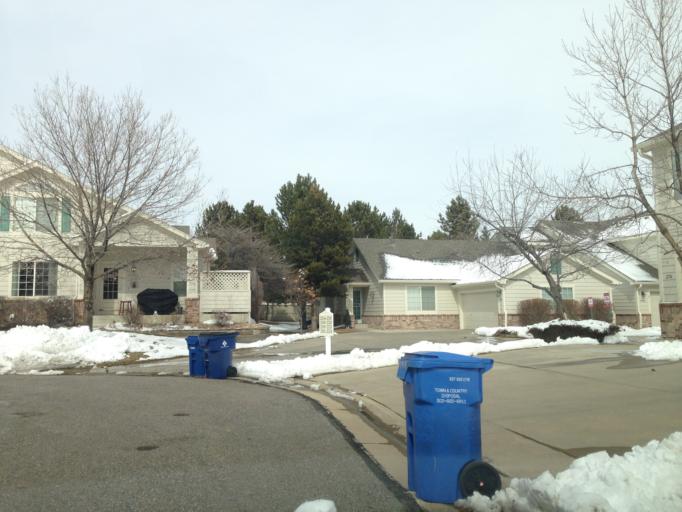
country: US
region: Colorado
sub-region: Boulder County
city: Lafayette
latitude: 39.9714
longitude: -105.0924
